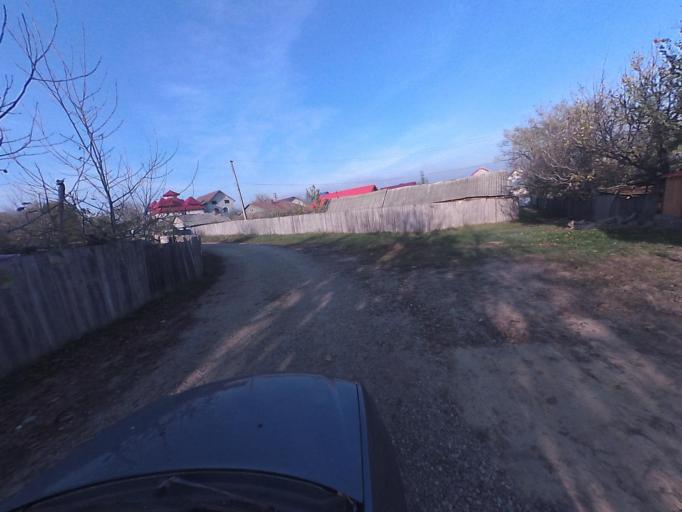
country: RO
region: Vaslui
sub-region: Comuna Bacesti
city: Bacesti
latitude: 46.8237
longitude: 27.2458
